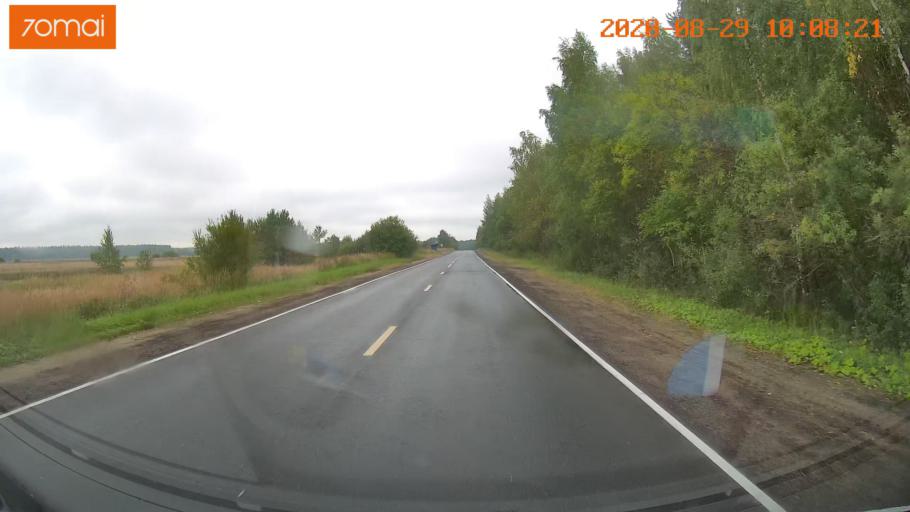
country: RU
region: Ivanovo
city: Kuznechikha
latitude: 57.3762
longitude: 42.5878
